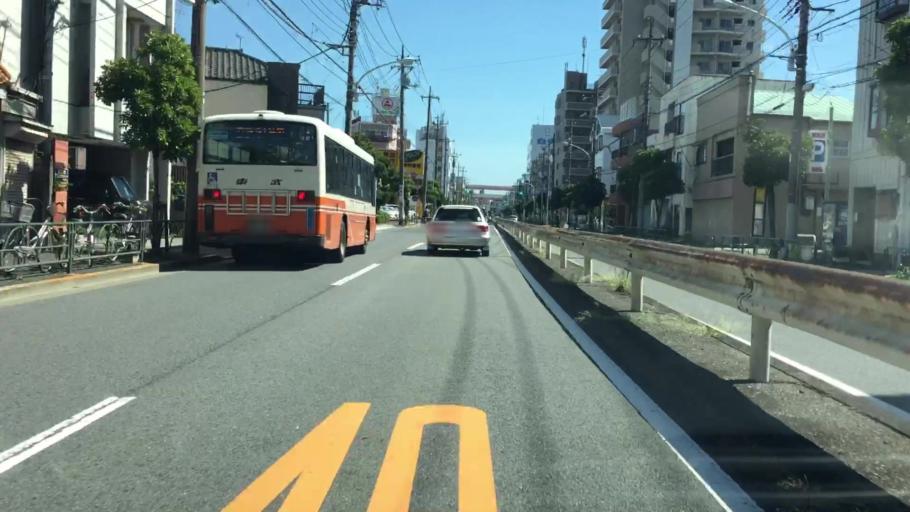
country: JP
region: Saitama
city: Soka
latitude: 35.7686
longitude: 139.7859
